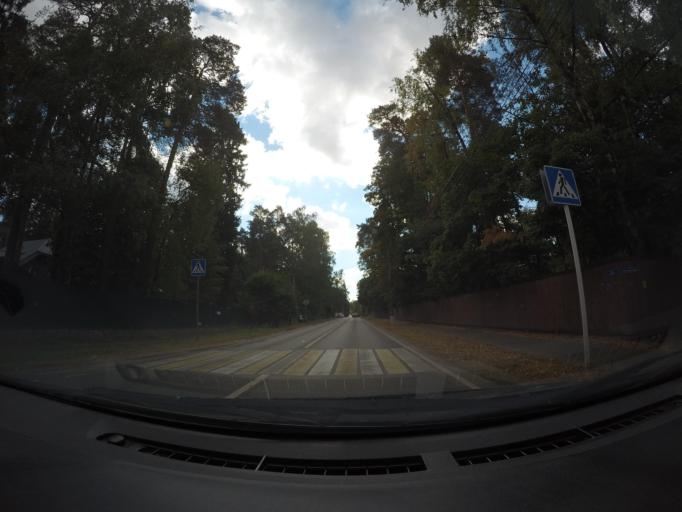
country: RU
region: Moskovskaya
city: Il'inskiy
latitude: 55.6240
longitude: 38.1137
